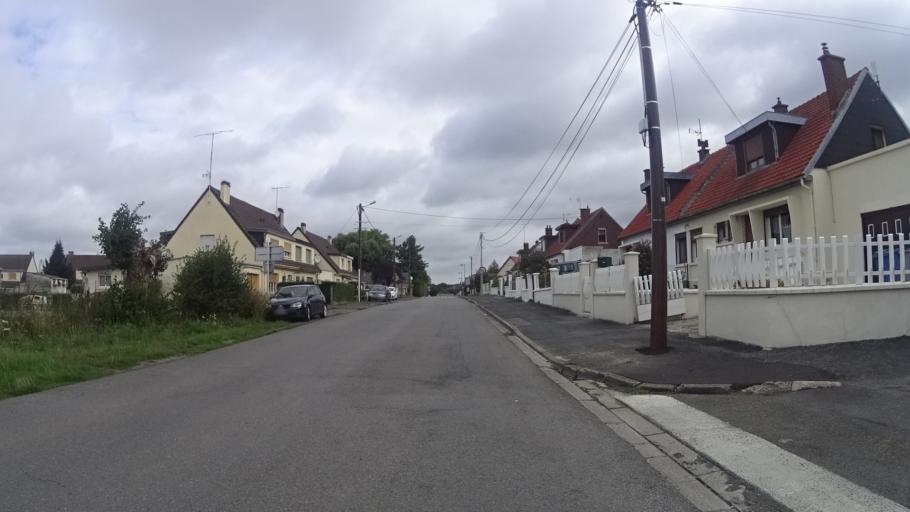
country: FR
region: Picardie
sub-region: Departement de l'Aisne
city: Boue
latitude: 50.0056
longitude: 3.6926
